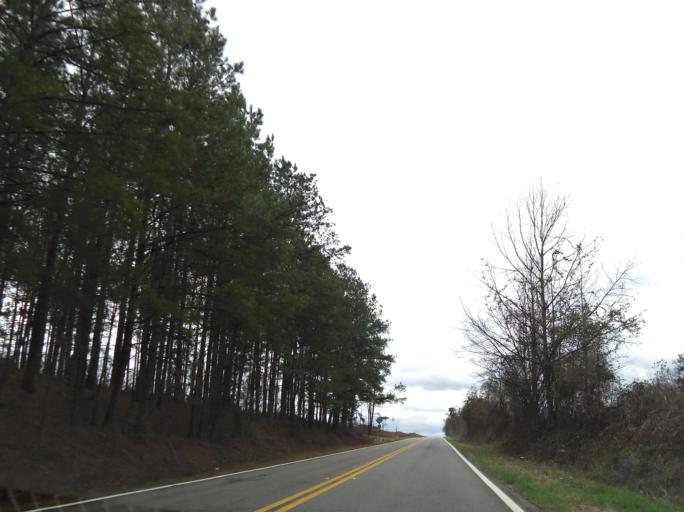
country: US
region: Georgia
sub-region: Twiggs County
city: Jeffersonville
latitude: 32.5494
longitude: -83.3740
